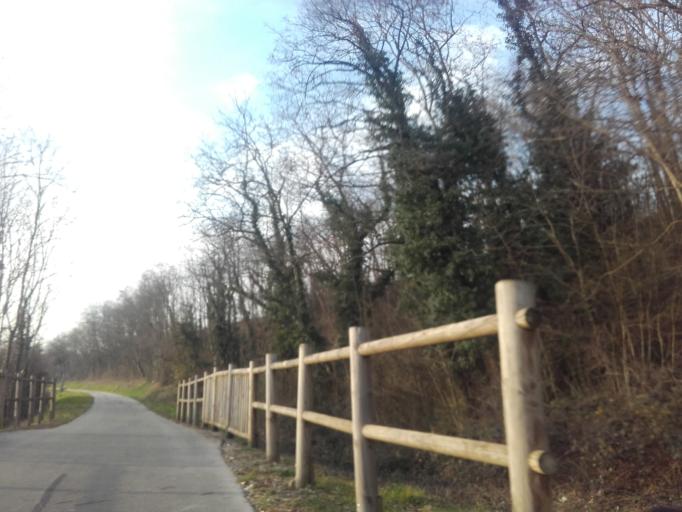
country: FR
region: Bourgogne
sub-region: Departement de la Cote-d'Or
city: Nolay
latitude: 46.9062
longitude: 4.6602
